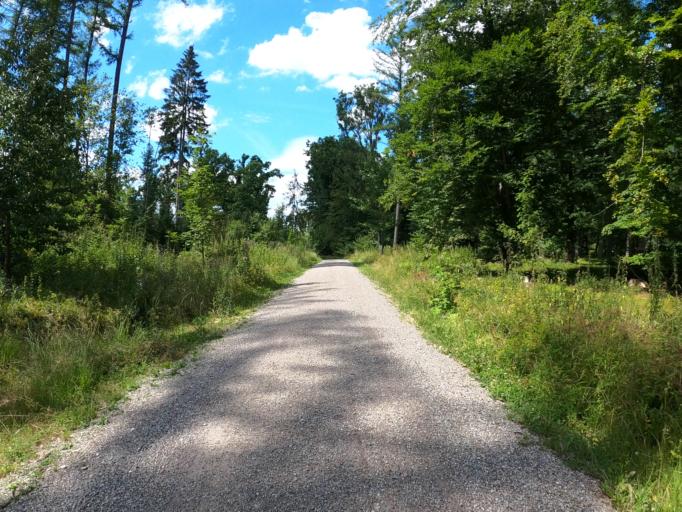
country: DE
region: Bavaria
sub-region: Swabia
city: Leipheim
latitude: 48.4201
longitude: 10.2105
